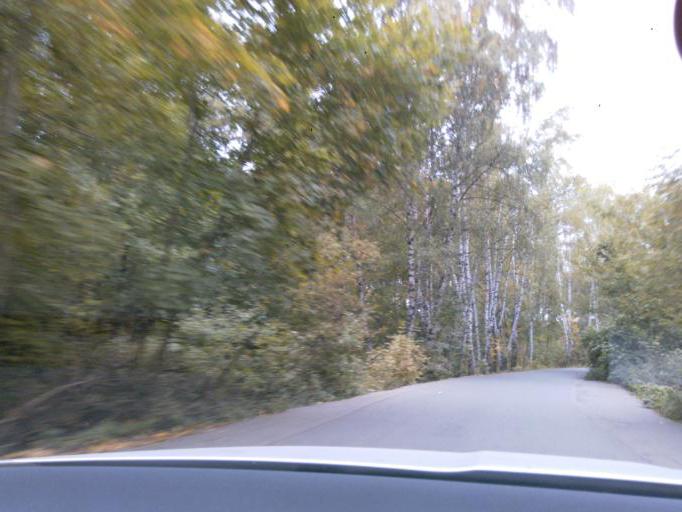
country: RU
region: Moskovskaya
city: Dolgoprudnyy
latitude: 55.9409
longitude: 37.5223
